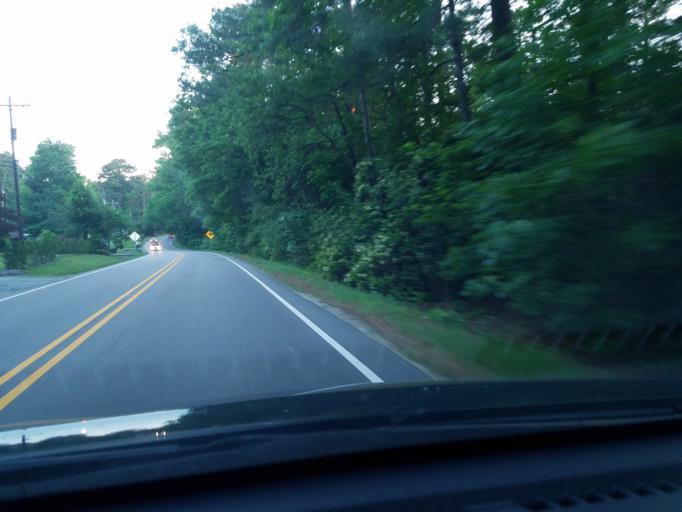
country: US
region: North Carolina
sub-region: Durham County
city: Durham
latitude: 35.9560
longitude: -78.9352
